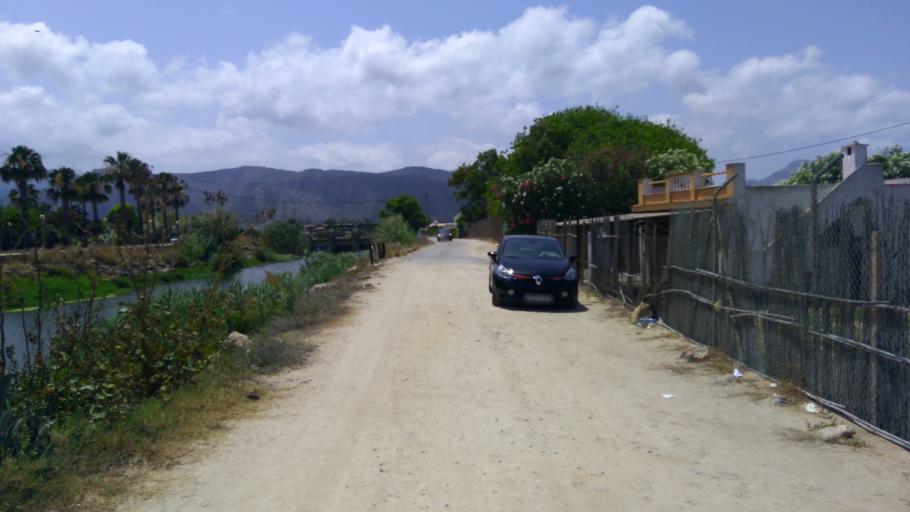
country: ES
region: Valencia
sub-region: Provincia de Valencia
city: Xeraco,Jaraco
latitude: 39.0582
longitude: -0.2005
